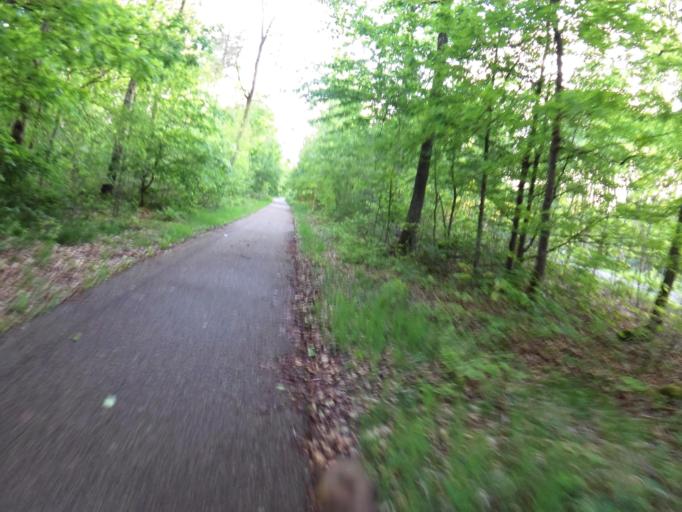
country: BE
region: Flanders
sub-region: Provincie Limburg
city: Zutendaal
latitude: 50.9505
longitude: 5.6059
